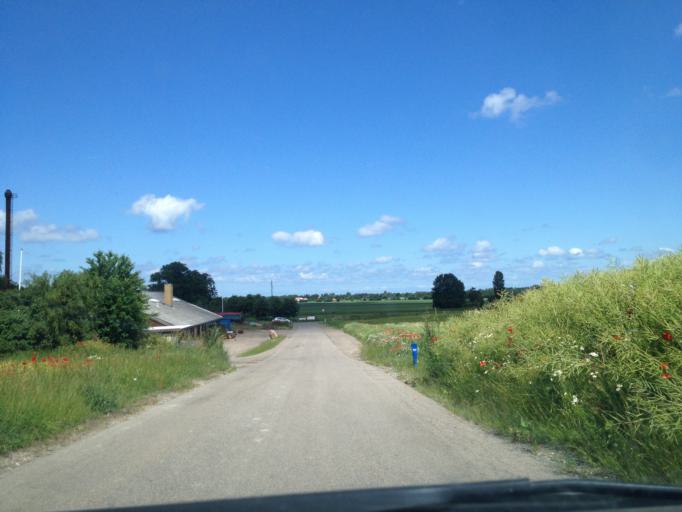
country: DK
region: Zealand
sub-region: Odsherred Kommune
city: Hojby
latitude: 55.9309
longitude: 11.5857
